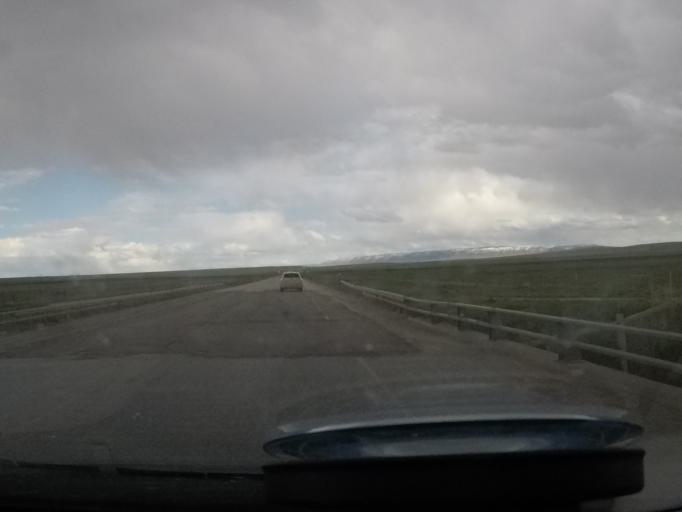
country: US
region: Wyoming
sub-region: Natrona County
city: Mills
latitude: 42.9530
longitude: -106.6404
